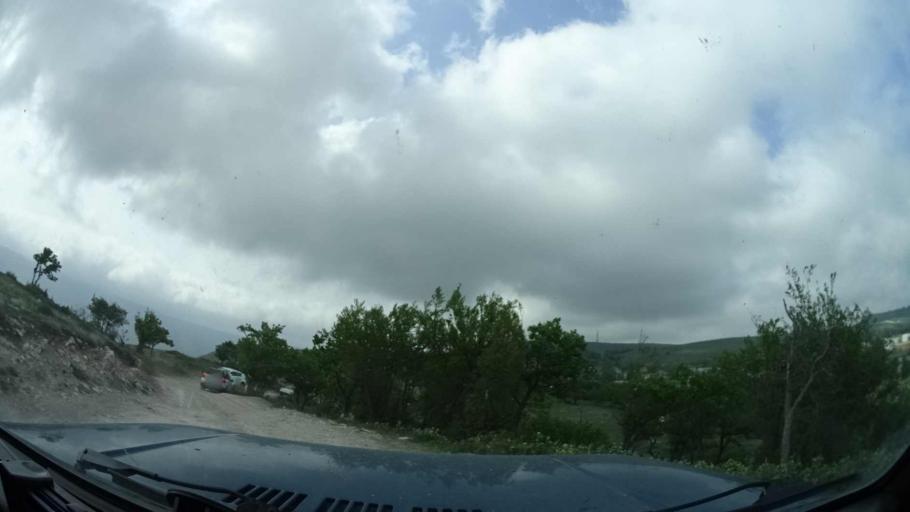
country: RU
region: Dagestan
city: Dubki
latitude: 43.0182
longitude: 46.8330
